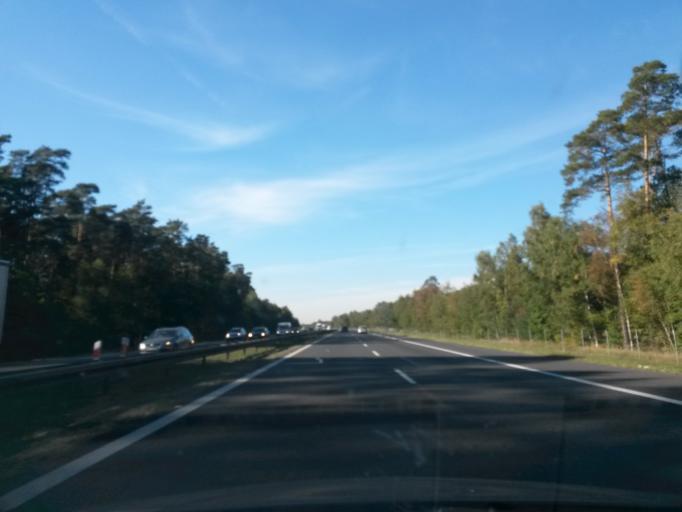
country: PL
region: Opole Voivodeship
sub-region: Powiat brzeski
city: Lewin Brzeski
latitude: 50.6995
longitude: 17.6204
